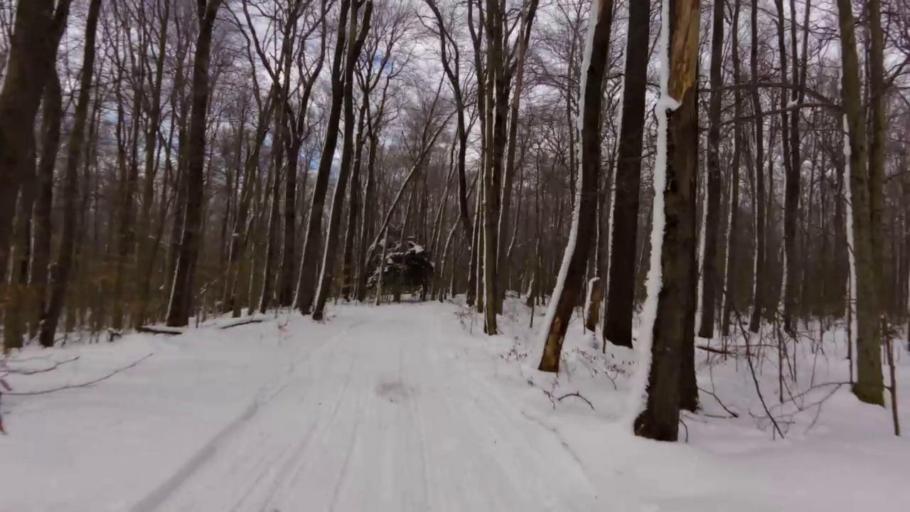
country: US
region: New York
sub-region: Cattaraugus County
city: Salamanca
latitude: 42.0365
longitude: -78.7535
